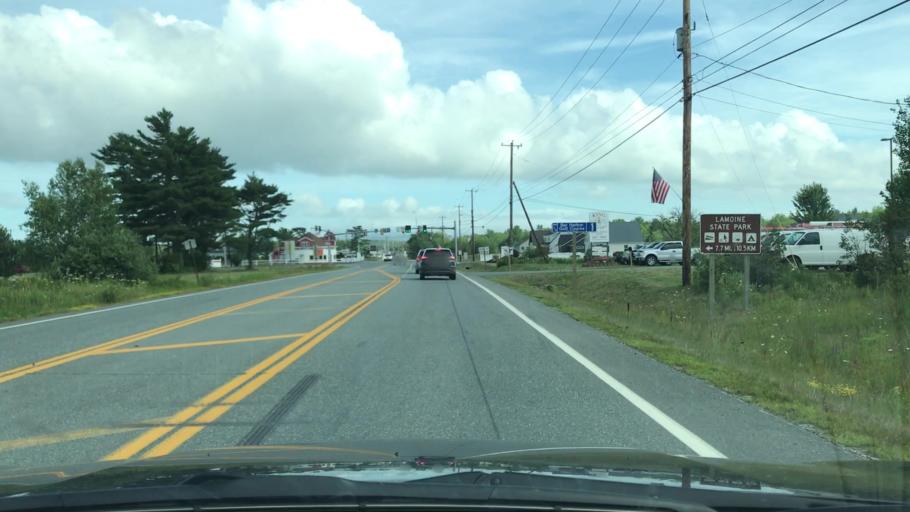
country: US
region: Maine
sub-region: Hancock County
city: Trenton
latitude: 44.4896
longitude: -68.3721
